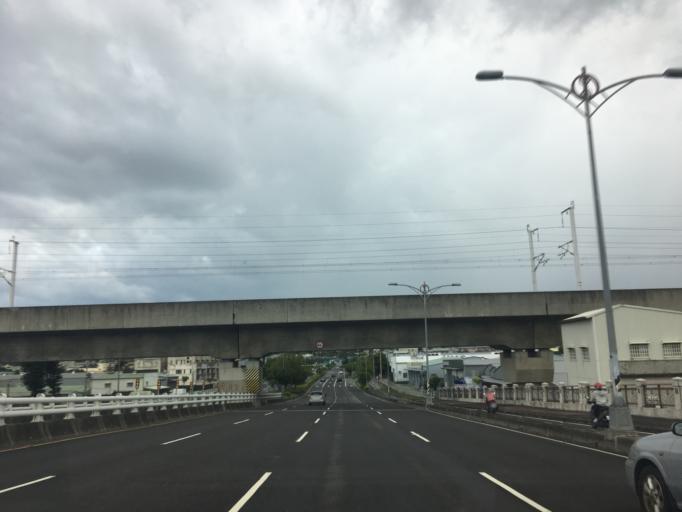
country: TW
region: Taiwan
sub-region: Taichung City
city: Taichung
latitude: 24.2038
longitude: 120.6370
